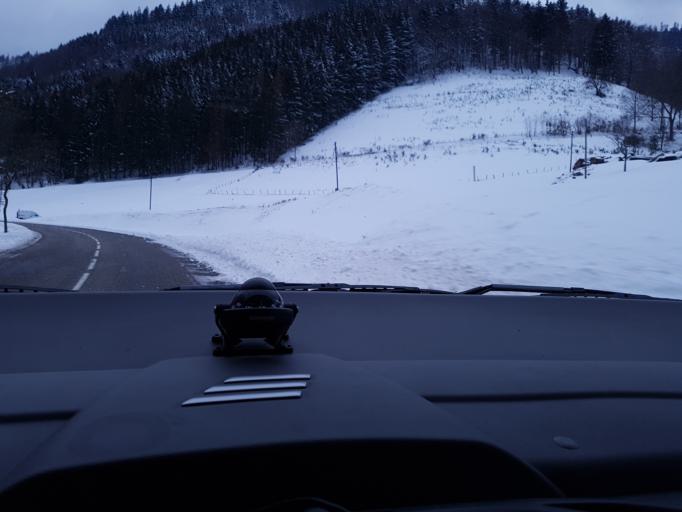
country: FR
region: Alsace
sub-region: Departement du Haut-Rhin
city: Sainte-Marie-aux-Mines
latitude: 48.2088
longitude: 7.1315
